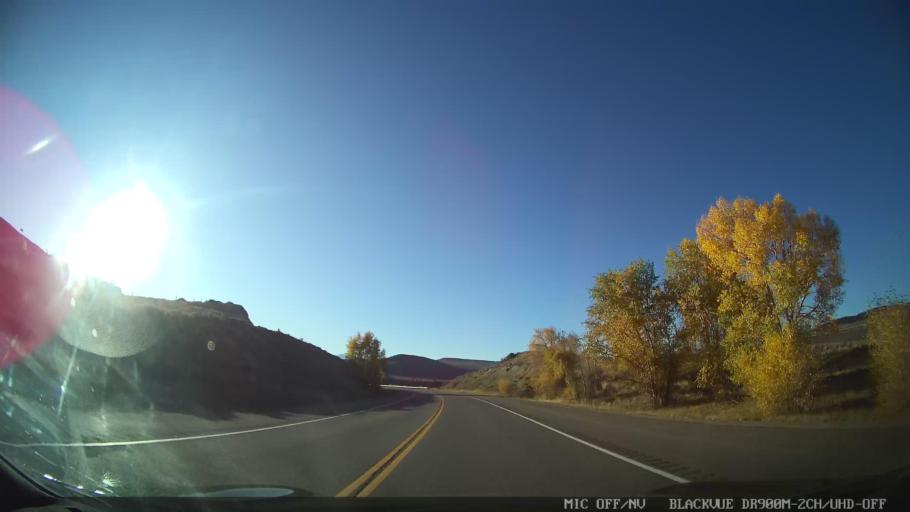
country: US
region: Colorado
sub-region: Grand County
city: Hot Sulphur Springs
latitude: 40.0545
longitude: -106.1737
